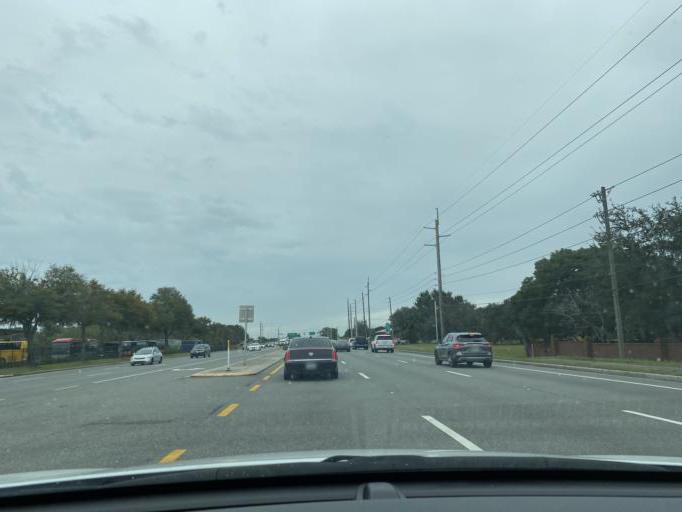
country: US
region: Florida
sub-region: Orange County
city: Oakland
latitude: 28.5465
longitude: -81.6471
